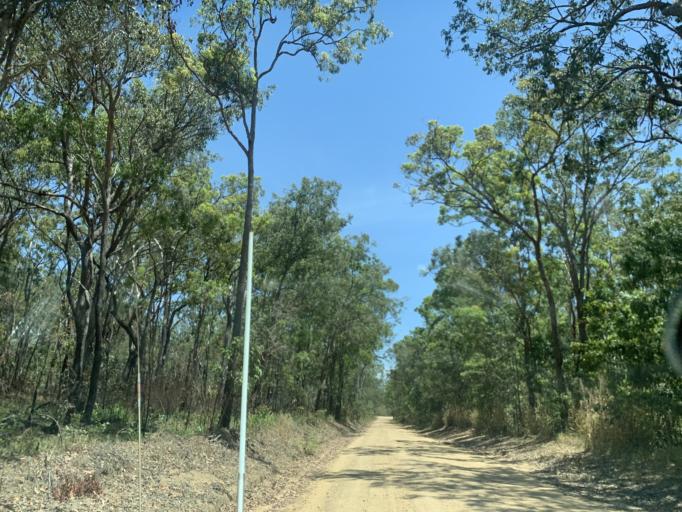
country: AU
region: Queensland
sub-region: Tablelands
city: Kuranda
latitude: -16.9202
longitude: 145.5910
